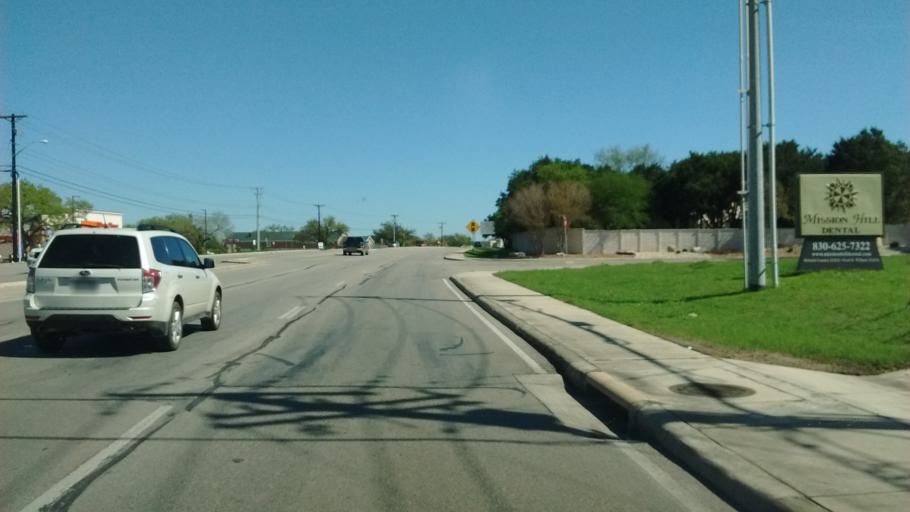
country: US
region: Texas
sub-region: Comal County
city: New Braunfels
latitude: 29.7193
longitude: -98.1644
